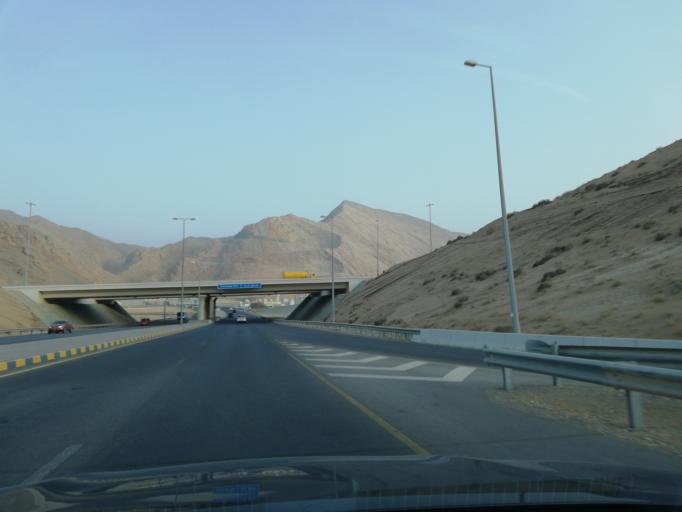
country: OM
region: Muhafazat Masqat
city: Bawshar
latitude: 23.5732
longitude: 58.4247
